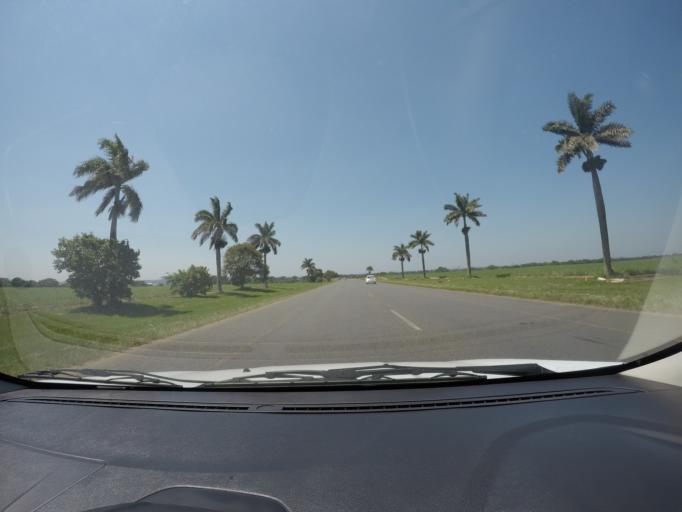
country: ZA
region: KwaZulu-Natal
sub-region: uThungulu District Municipality
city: Empangeni
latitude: -28.8056
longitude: 31.9572
